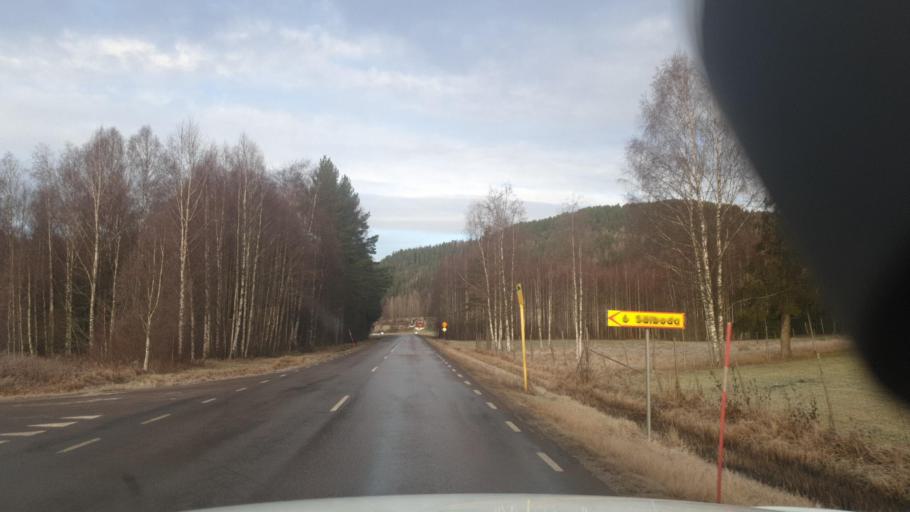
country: SE
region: Vaermland
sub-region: Arvika Kommun
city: Arvika
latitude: 59.7456
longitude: 12.6391
